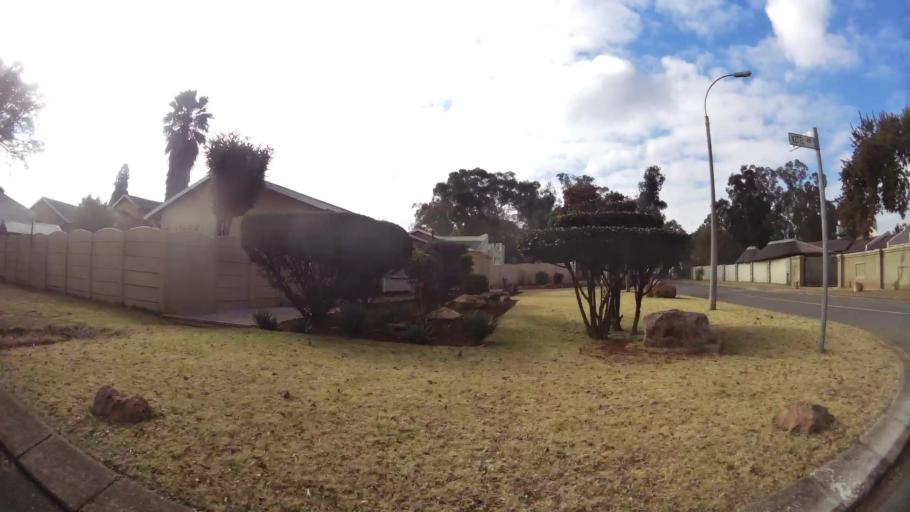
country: ZA
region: Gauteng
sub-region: City of Johannesburg Metropolitan Municipality
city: Roodepoort
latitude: -26.2021
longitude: 27.9169
